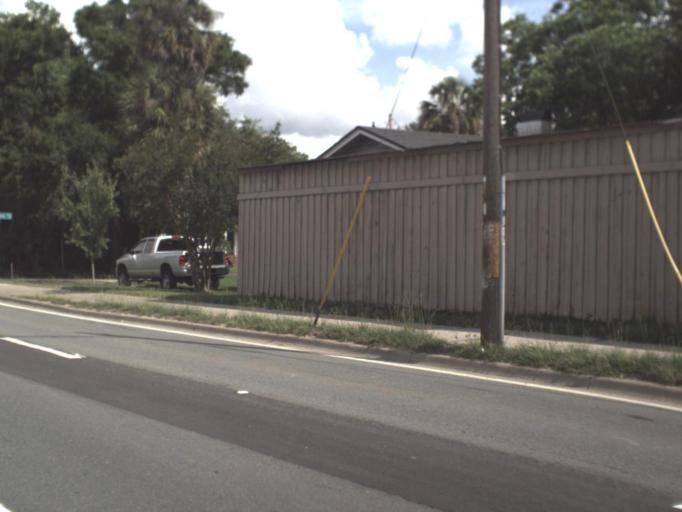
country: US
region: Florida
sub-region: Duval County
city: Jacksonville
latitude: 30.3080
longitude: -81.6434
